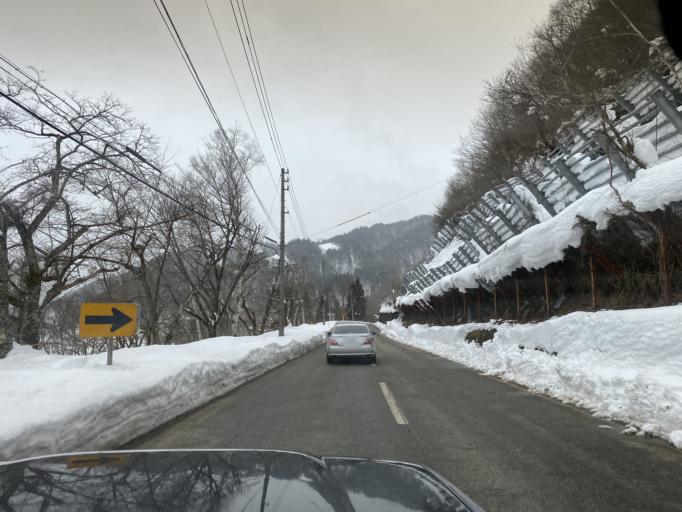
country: JP
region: Gifu
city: Takayama
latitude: 36.0965
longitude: 136.9360
